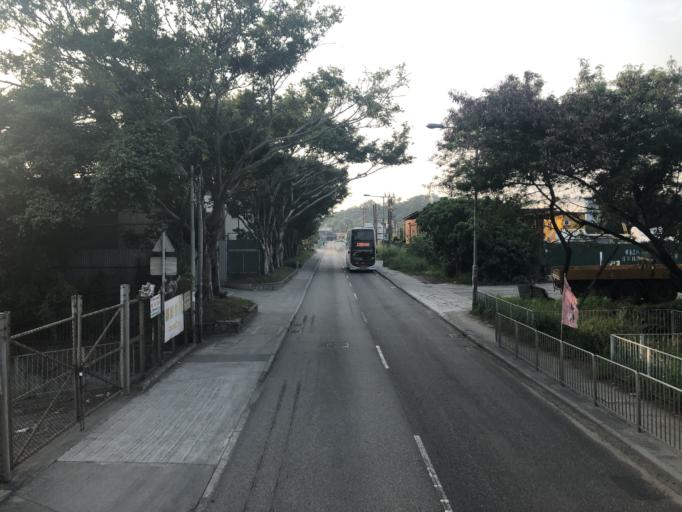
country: HK
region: Yuen Long
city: Yuen Long Kau Hui
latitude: 22.4651
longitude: 113.9858
